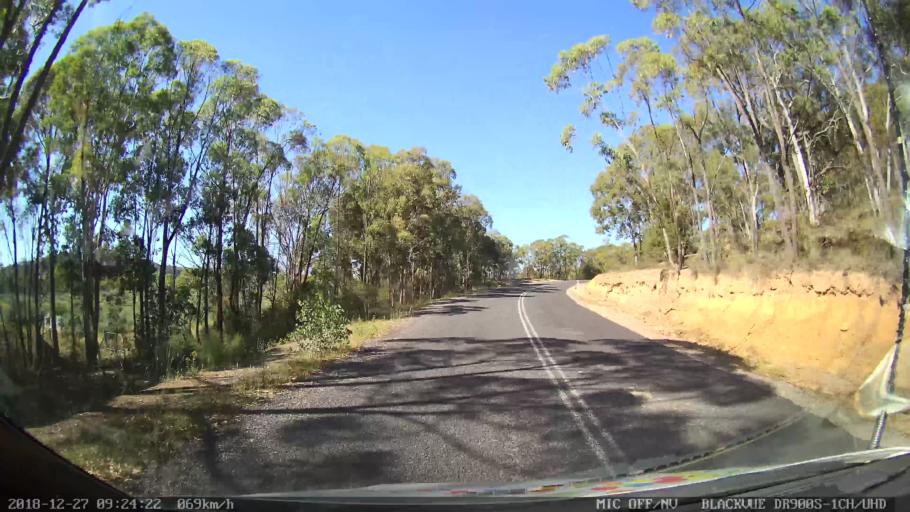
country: AU
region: New South Wales
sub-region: Lithgow
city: Portland
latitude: -33.1359
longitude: 149.9977
